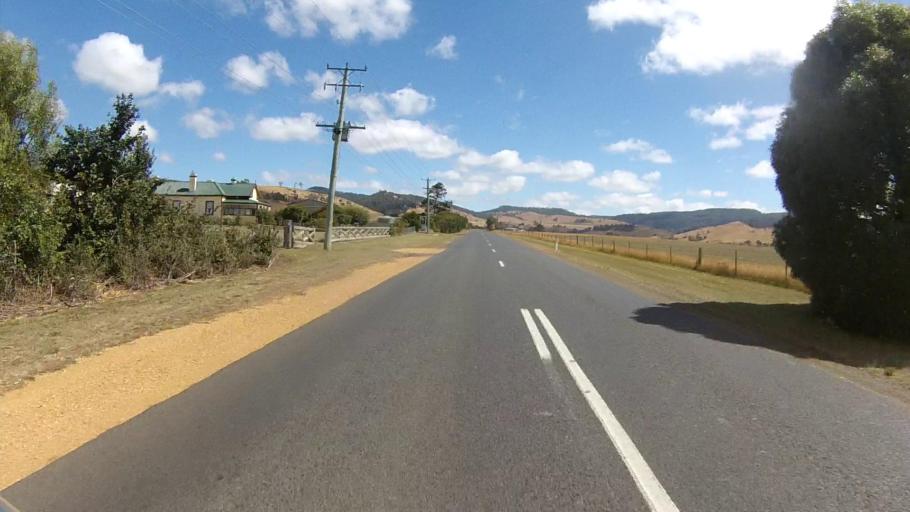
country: AU
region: Tasmania
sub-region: Brighton
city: Bridgewater
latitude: -42.5320
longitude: 147.3622
